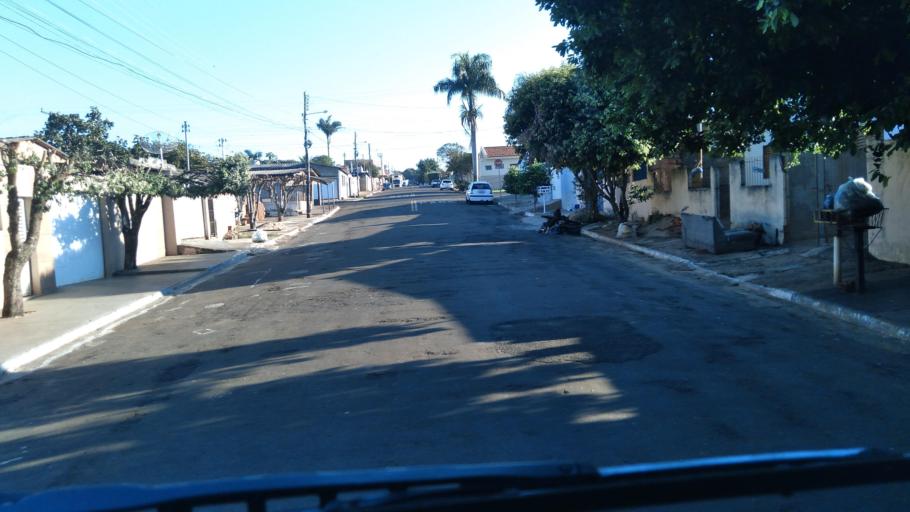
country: BR
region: Goias
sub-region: Mineiros
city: Mineiros
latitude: -17.5761
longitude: -52.5650
